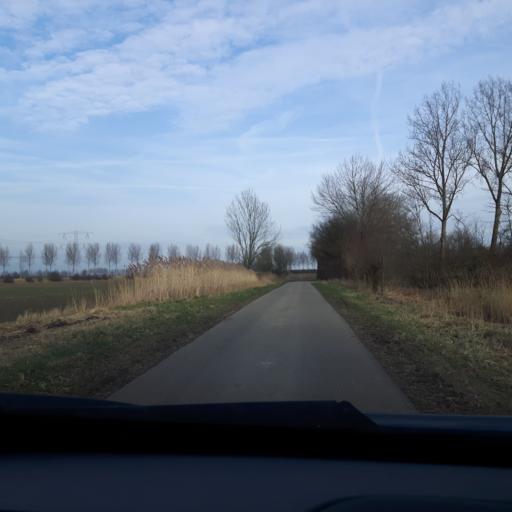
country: NL
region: Zeeland
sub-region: Gemeente Goes
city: Goes
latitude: 51.4412
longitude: 3.9130
